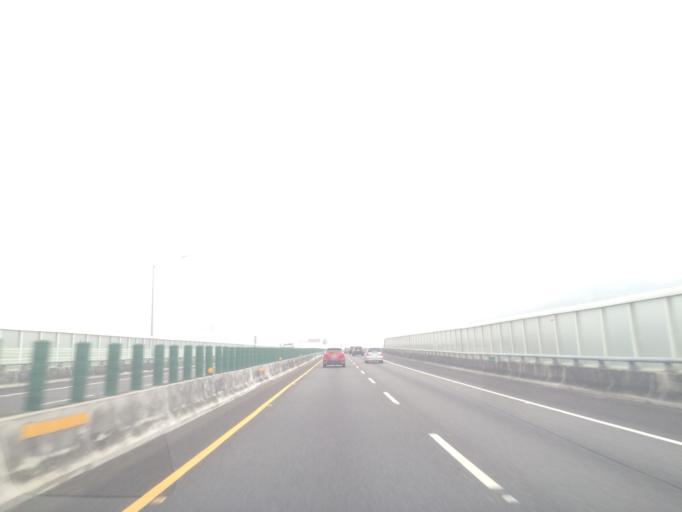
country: TW
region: Taiwan
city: Zhongxing New Village
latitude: 24.0103
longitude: 120.7025
